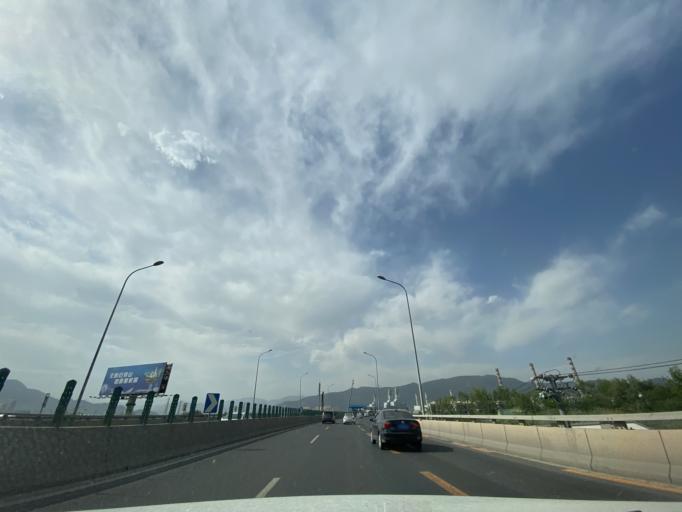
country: CN
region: Beijing
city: Guangning
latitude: 39.9324
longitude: 116.1265
